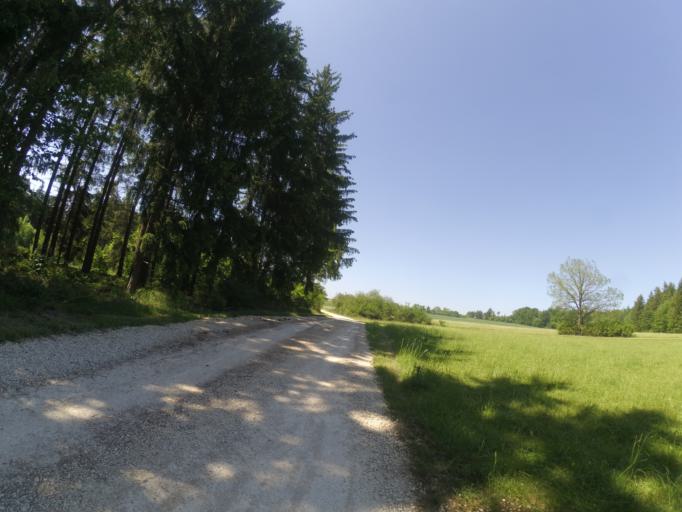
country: DE
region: Baden-Wuerttemberg
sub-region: Tuebingen Region
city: Merklingen
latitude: 48.4959
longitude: 9.7855
